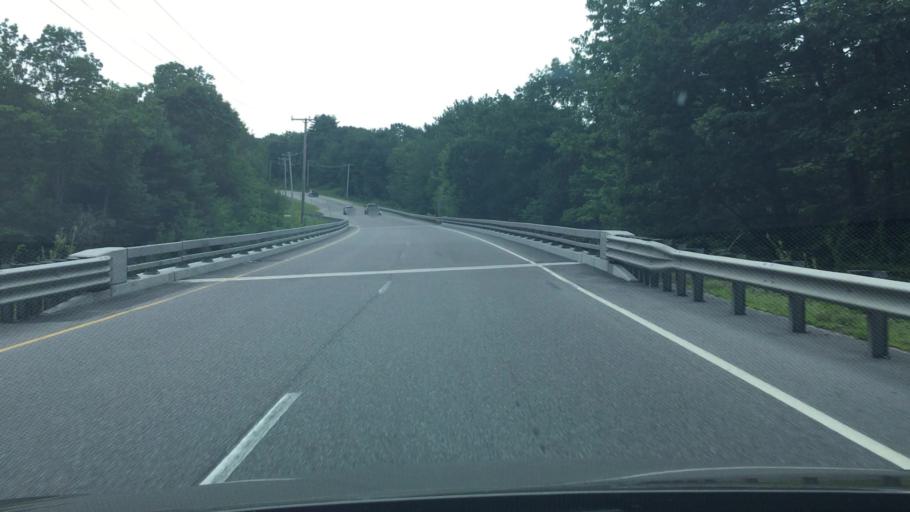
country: US
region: Maine
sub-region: Androscoggin County
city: Auburn
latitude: 44.0599
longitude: -70.2555
